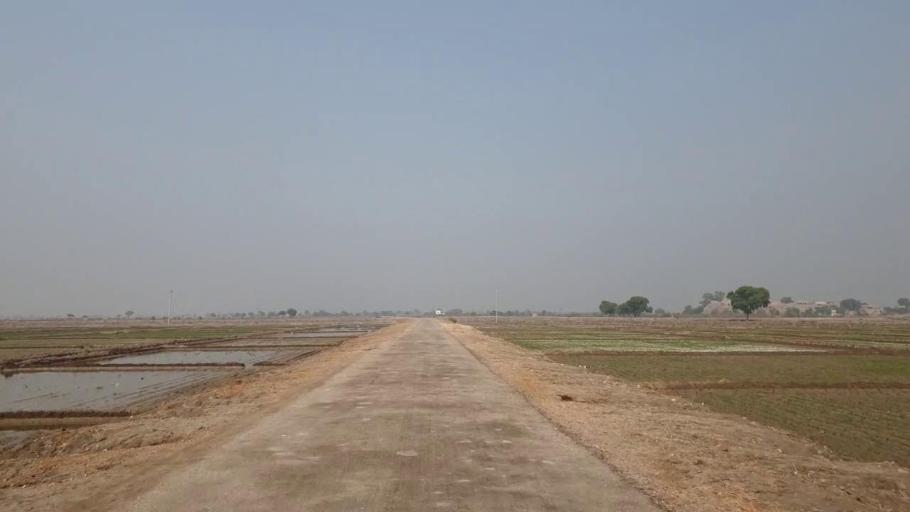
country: PK
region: Sindh
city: Bhan
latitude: 26.4829
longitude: 67.7017
